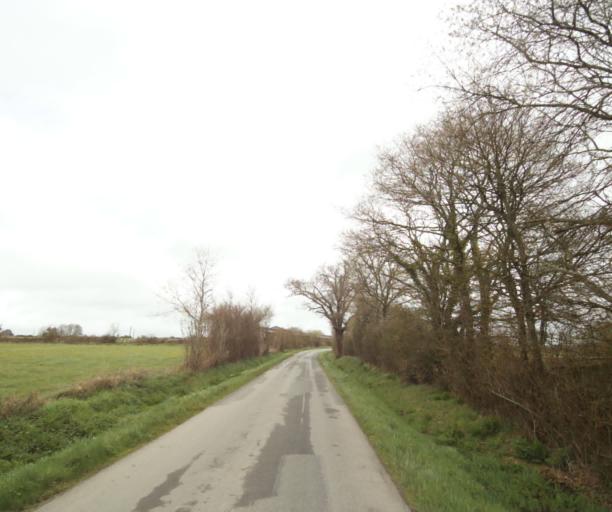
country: FR
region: Pays de la Loire
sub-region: Departement de la Loire-Atlantique
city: Bouvron
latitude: 47.4291
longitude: -1.8979
